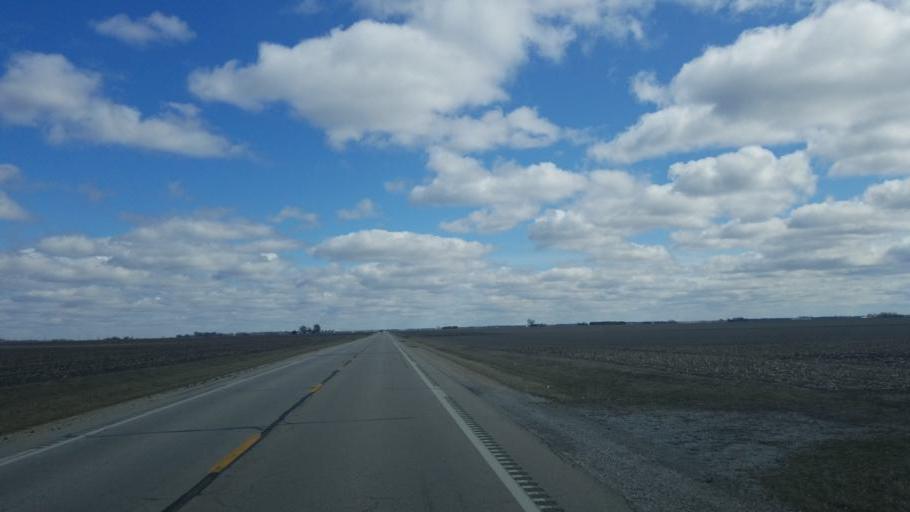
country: US
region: Illinois
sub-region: Douglas County
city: Villa Grove
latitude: 39.7918
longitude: -88.1423
